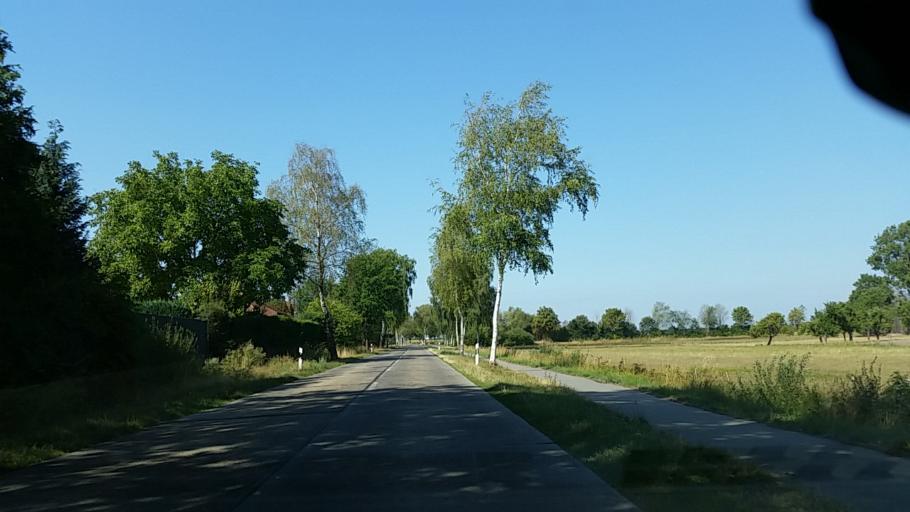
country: DE
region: Lower Saxony
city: Wahrenholz
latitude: 52.6157
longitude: 10.5962
